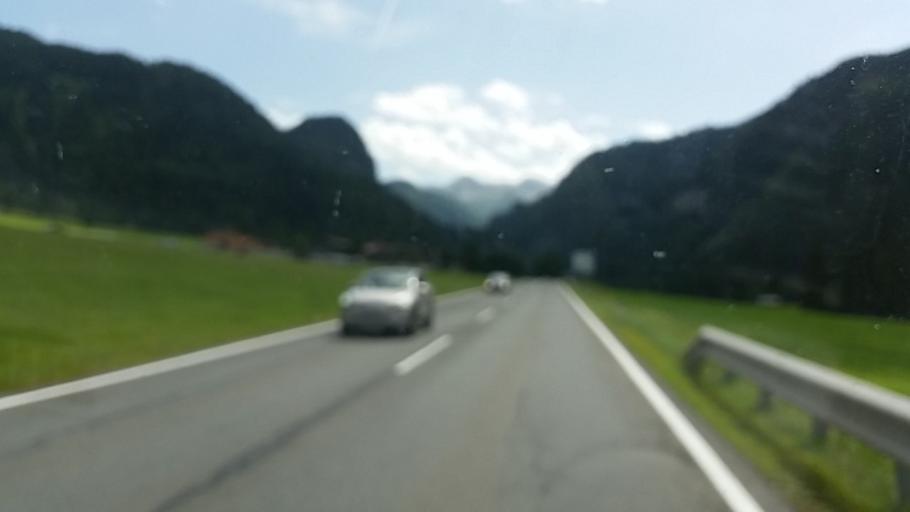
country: AT
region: Salzburg
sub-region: Politischer Bezirk Sankt Johann im Pongau
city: Untertauern
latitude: 47.3099
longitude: 13.5072
